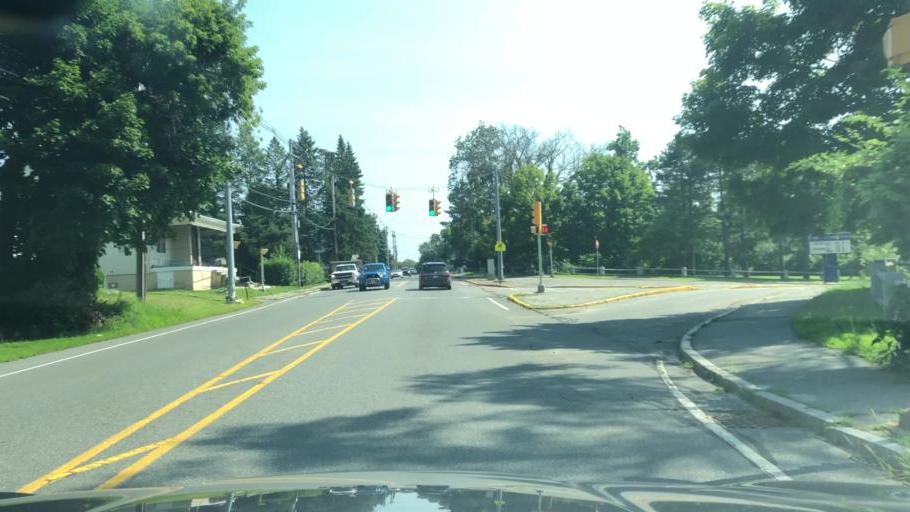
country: US
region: Massachusetts
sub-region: Essex County
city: Methuen
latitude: 42.7488
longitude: -71.1723
